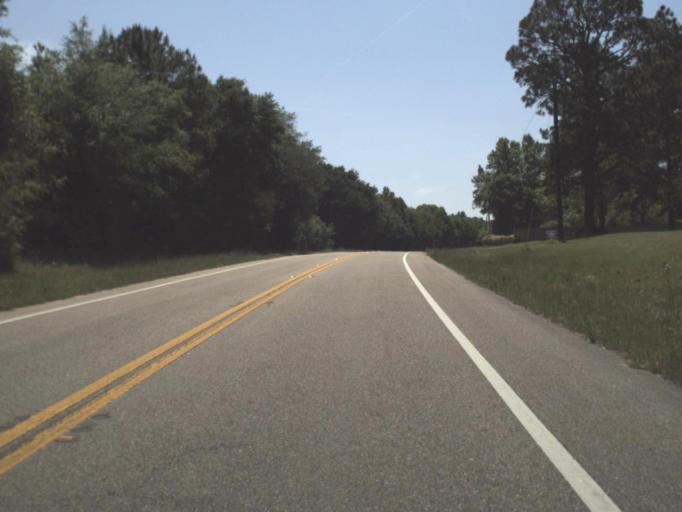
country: US
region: Florida
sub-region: Jackson County
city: Marianna
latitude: 30.6608
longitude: -85.2212
